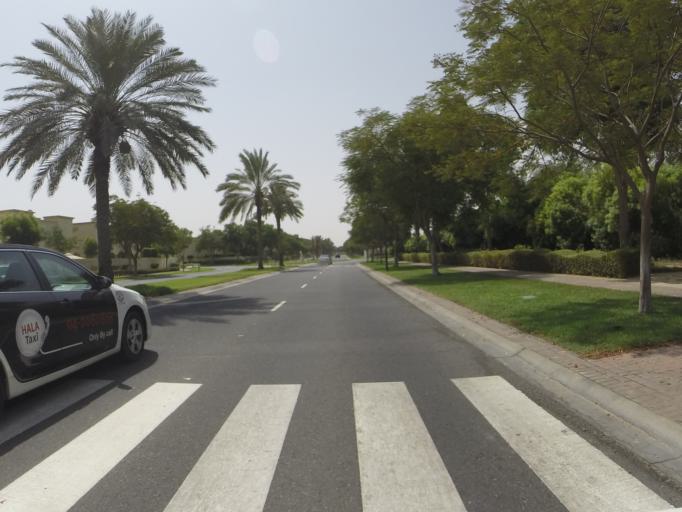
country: AE
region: Dubai
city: Dubai
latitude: 25.0591
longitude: 55.1614
